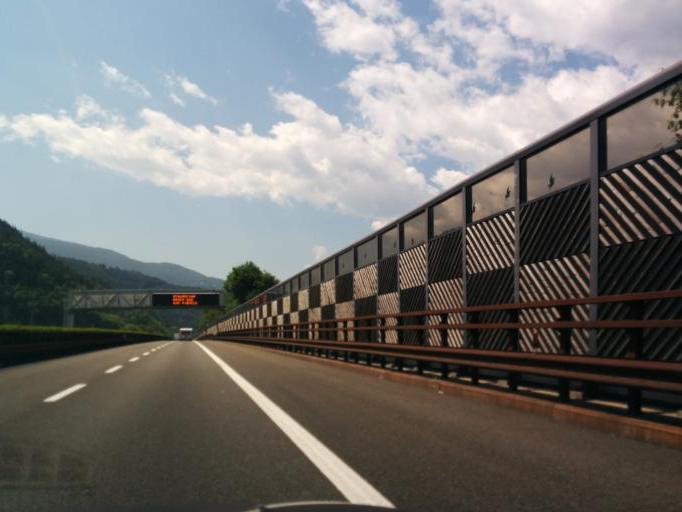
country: IT
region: Trentino-Alto Adige
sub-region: Bolzano
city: Velturno
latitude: 46.6701
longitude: 11.6165
